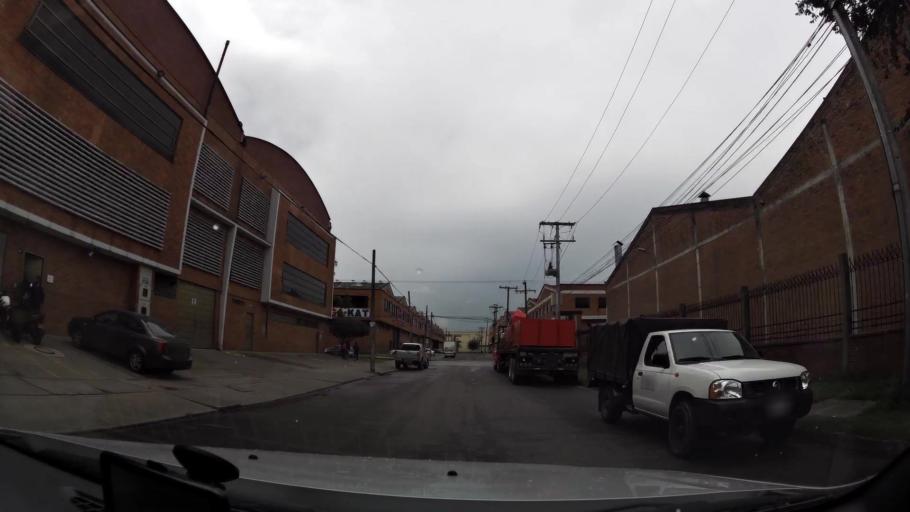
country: CO
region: Bogota D.C.
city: Bogota
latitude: 4.6482
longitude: -74.1230
